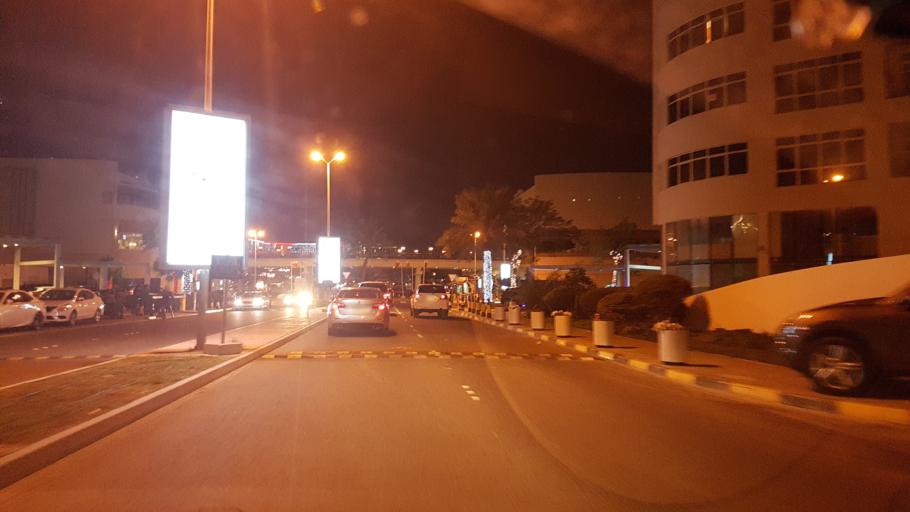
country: BH
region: Muharraq
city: Al Hadd
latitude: 26.2911
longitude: 50.6649
